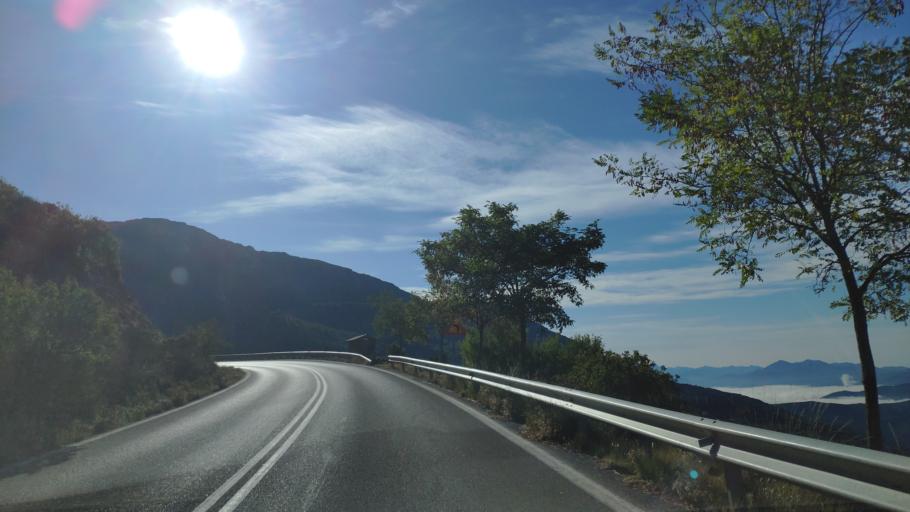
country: GR
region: Peloponnese
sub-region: Nomos Arkadias
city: Dimitsana
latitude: 37.5832
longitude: 22.0493
